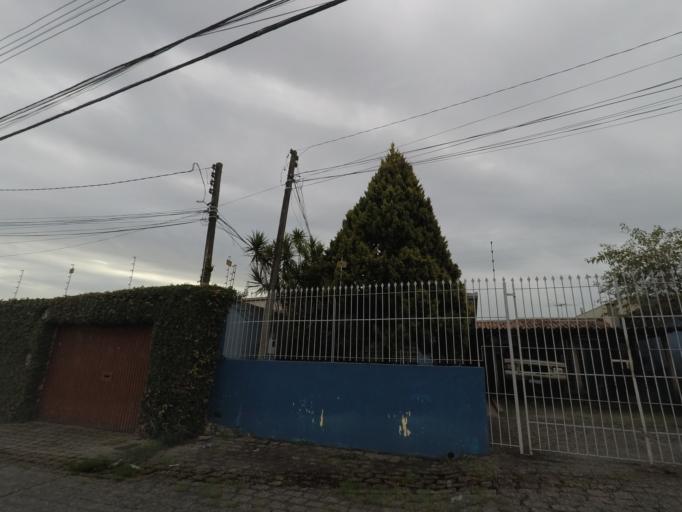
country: BR
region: Parana
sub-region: Curitiba
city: Curitiba
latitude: -25.4406
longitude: -49.2497
